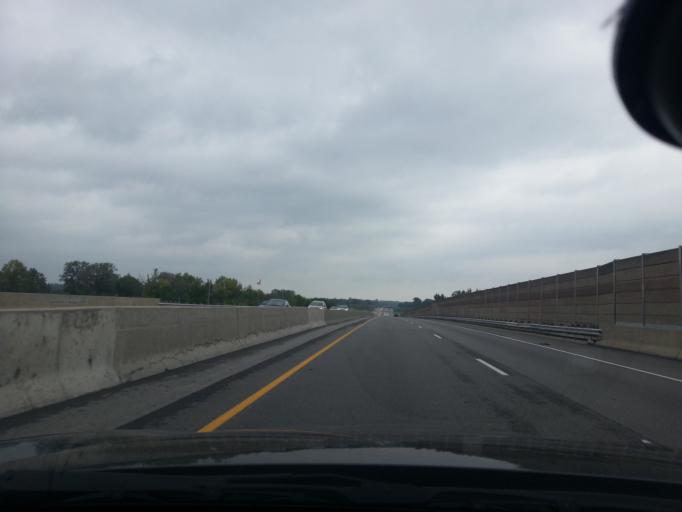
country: CA
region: Ontario
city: Brockville
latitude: 44.6053
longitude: -75.6932
